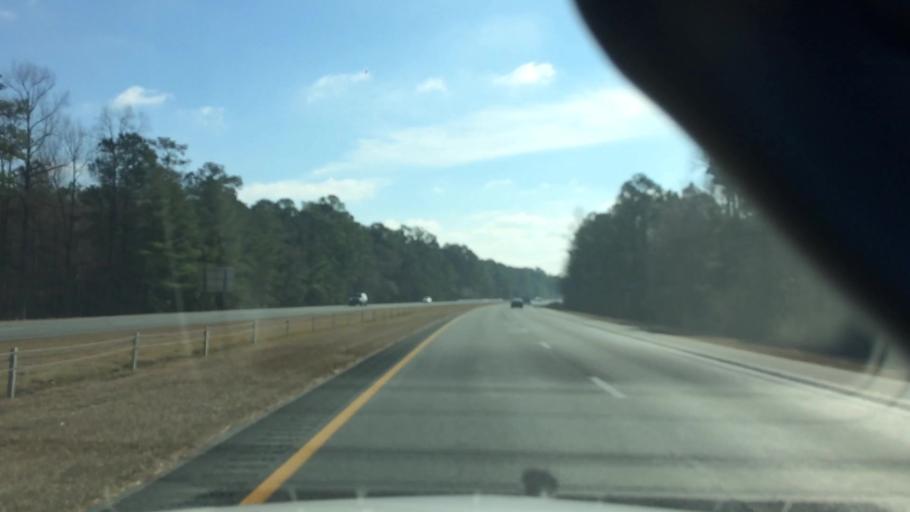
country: US
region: North Carolina
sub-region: Duplin County
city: Wallace
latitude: 34.7488
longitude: -77.9460
